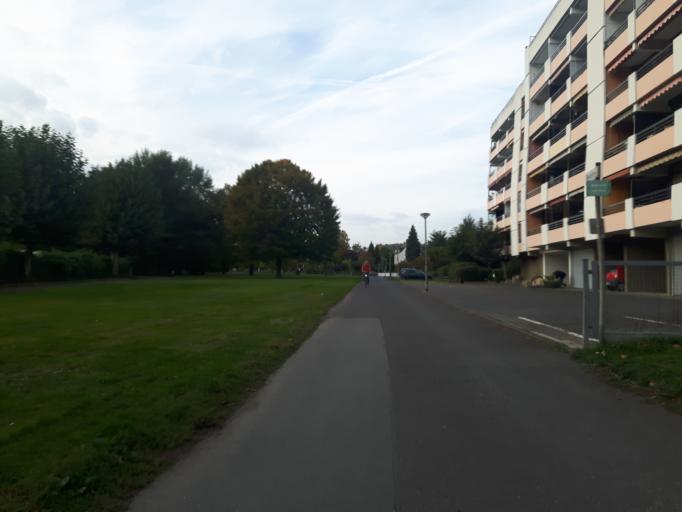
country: DE
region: Rheinland-Pfalz
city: Bad Honningen
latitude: 50.5105
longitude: 7.3108
